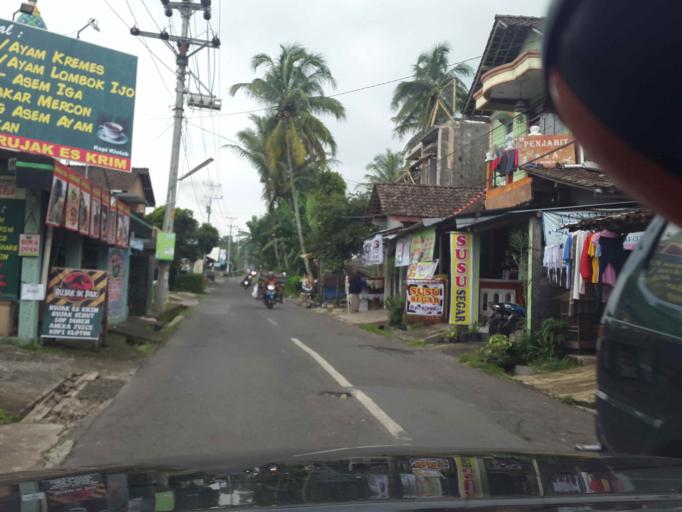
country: ID
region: Central Java
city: Salatiga
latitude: -7.3620
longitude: 110.5160
